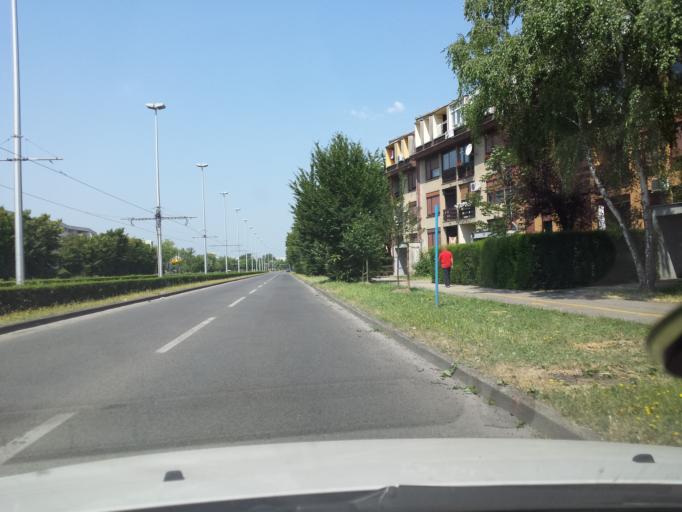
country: HR
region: Grad Zagreb
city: Jankomir
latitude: 45.7885
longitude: 15.9270
